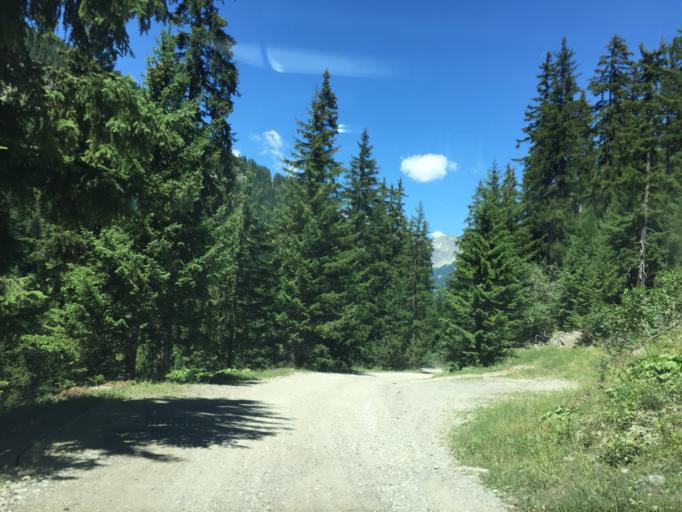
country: FR
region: Rhone-Alpes
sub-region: Departement de la Savoie
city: Modane
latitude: 45.1581
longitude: 6.6455
